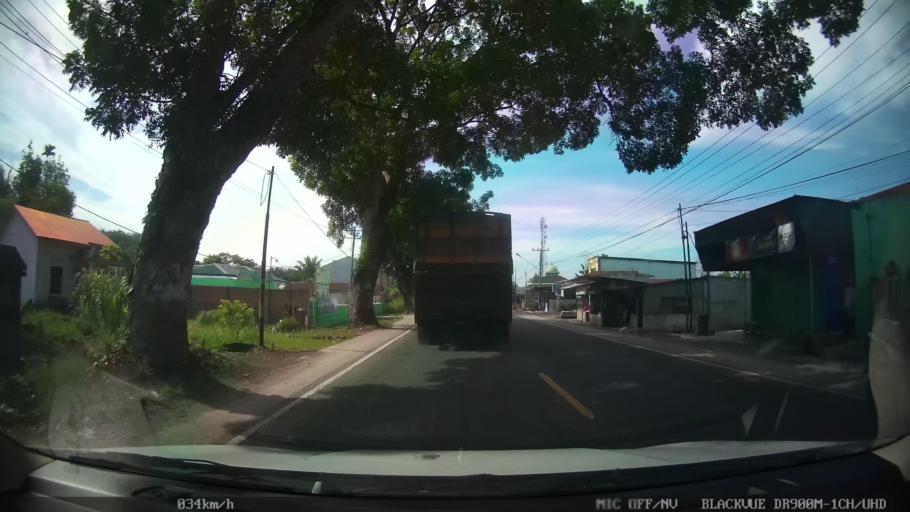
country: ID
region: North Sumatra
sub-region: Kabupaten Langkat
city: Stabat
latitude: 3.7055
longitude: 98.5062
